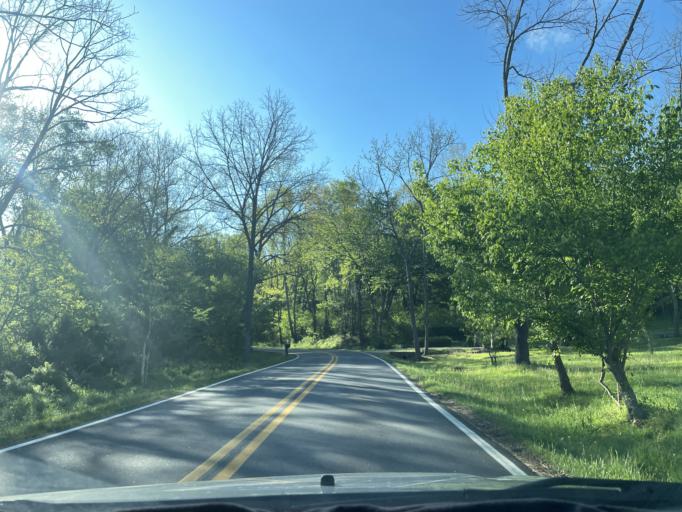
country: US
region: Maryland
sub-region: Carroll County
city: Mount Airy
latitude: 39.4190
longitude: -77.1452
